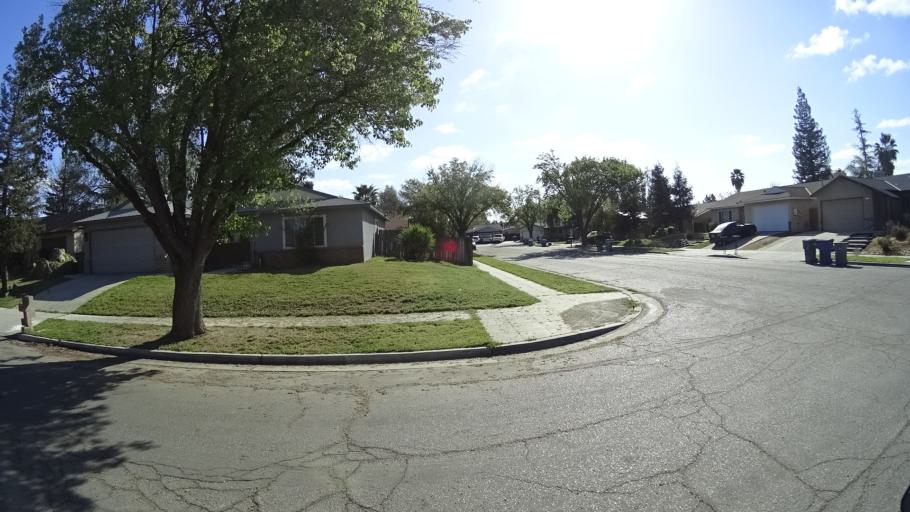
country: US
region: California
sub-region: Fresno County
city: West Park
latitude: 36.7976
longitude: -119.8765
